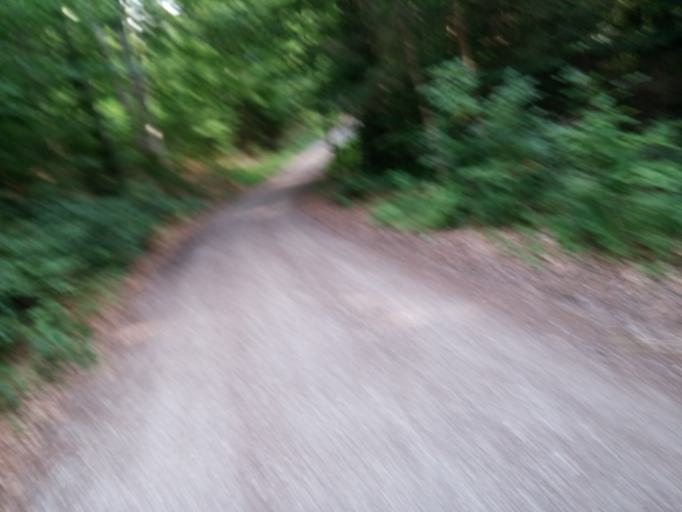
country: DE
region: Bavaria
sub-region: Upper Bavaria
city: Moosach
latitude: 48.0216
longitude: 11.8672
